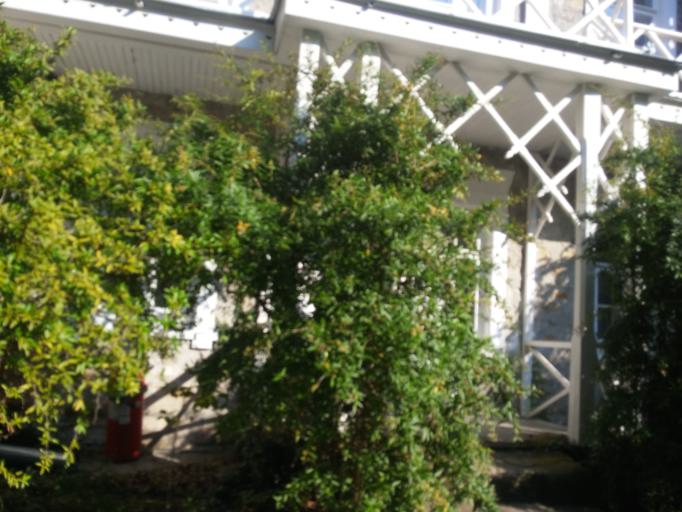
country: RU
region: Krasnodarskiy
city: Divnomorskoye
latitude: 44.4668
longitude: 38.1642
